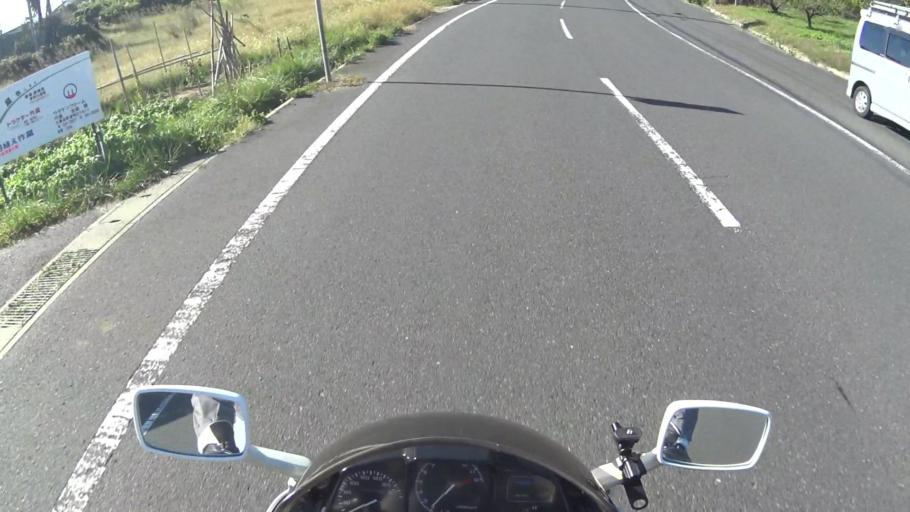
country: JP
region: Hyogo
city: Toyooka
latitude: 35.6273
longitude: 134.9283
